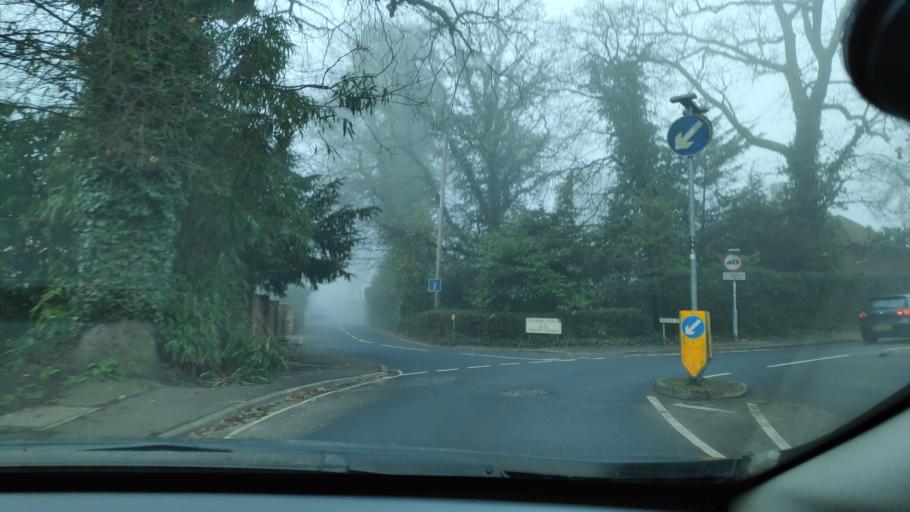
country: GB
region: England
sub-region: Hampshire
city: Farnborough
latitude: 51.2870
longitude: -0.7445
